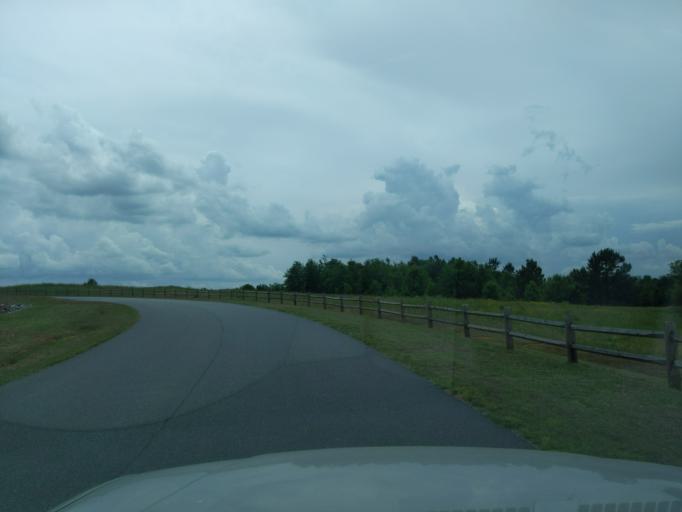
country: US
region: South Carolina
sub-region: Spartanburg County
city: Inman Mills
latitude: 35.0617
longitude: -82.1701
